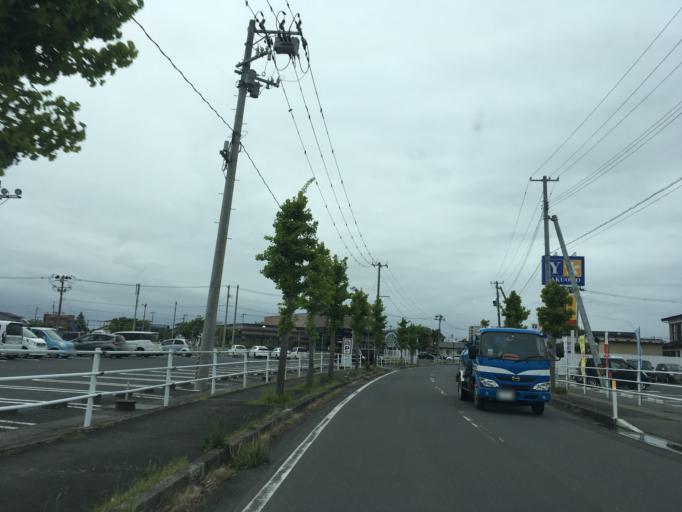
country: JP
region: Miyagi
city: Wakuya
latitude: 38.6801
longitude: 141.1921
